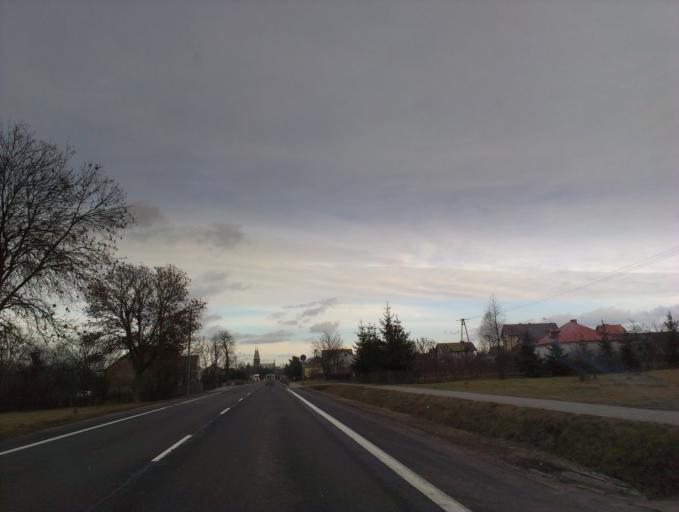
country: PL
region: Masovian Voivodeship
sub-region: Powiat sierpecki
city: Szczutowo
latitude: 52.9021
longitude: 19.5163
